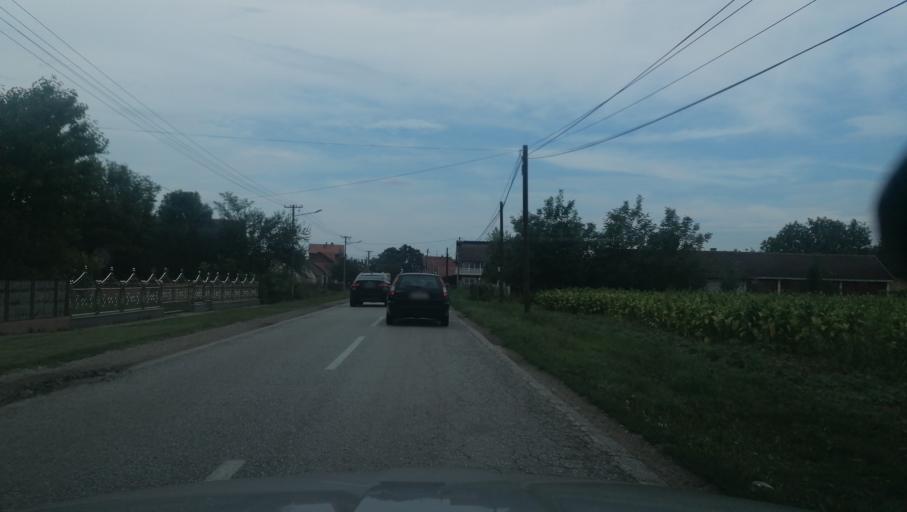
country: RS
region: Central Serbia
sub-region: Macvanski Okrug
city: Bogatic
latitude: 44.8325
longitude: 19.4698
